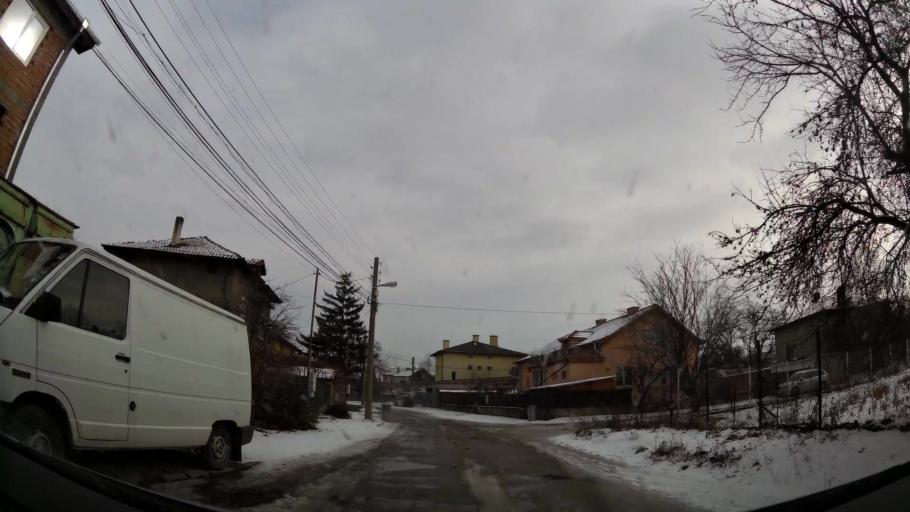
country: BG
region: Sofia-Capital
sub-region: Stolichna Obshtina
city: Sofia
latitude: 42.7140
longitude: 23.4092
